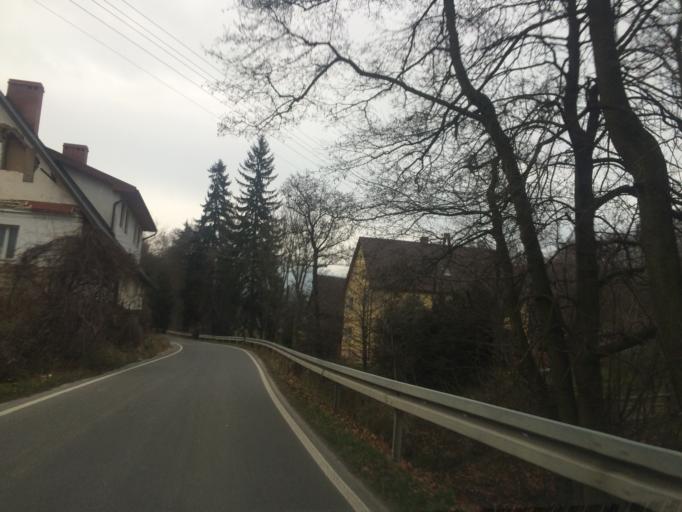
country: PL
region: Lower Silesian Voivodeship
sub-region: Powiat klodzki
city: Bystrzyca Klodzka
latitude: 50.2752
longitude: 16.7208
